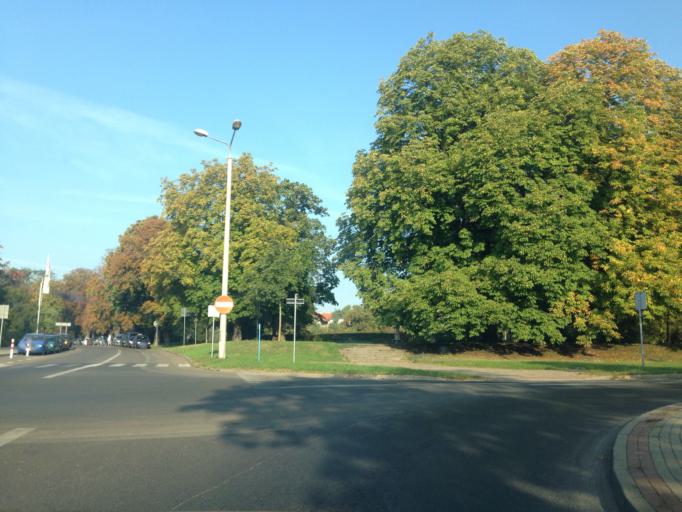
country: PL
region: Kujawsko-Pomorskie
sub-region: Torun
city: Torun
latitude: 53.0083
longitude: 18.5970
